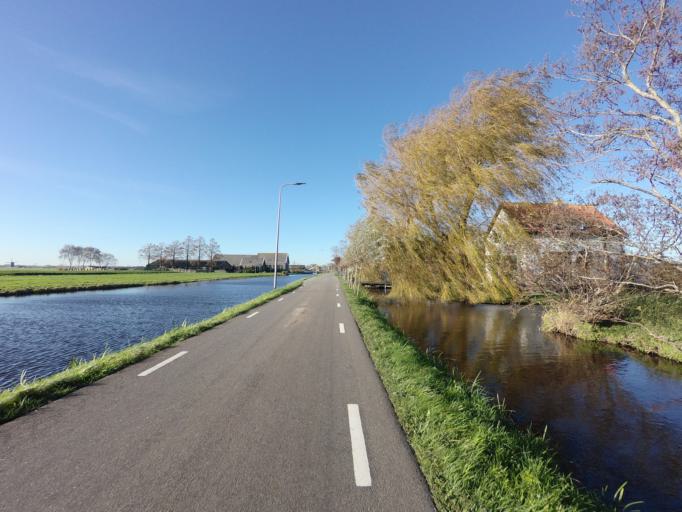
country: NL
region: South Holland
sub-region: Gemeente Nieuwkoop
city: Nieuwkoop
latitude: 52.1336
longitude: 4.7408
